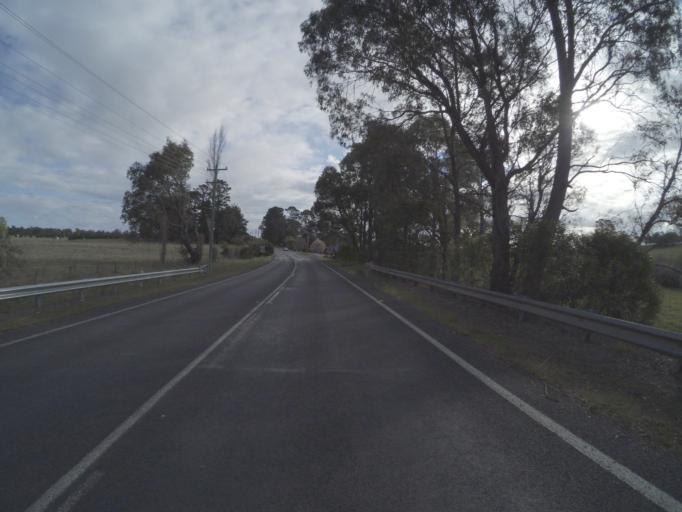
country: AU
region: New South Wales
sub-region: Wingecarribee
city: Moss Vale
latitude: -34.5722
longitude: 150.3151
